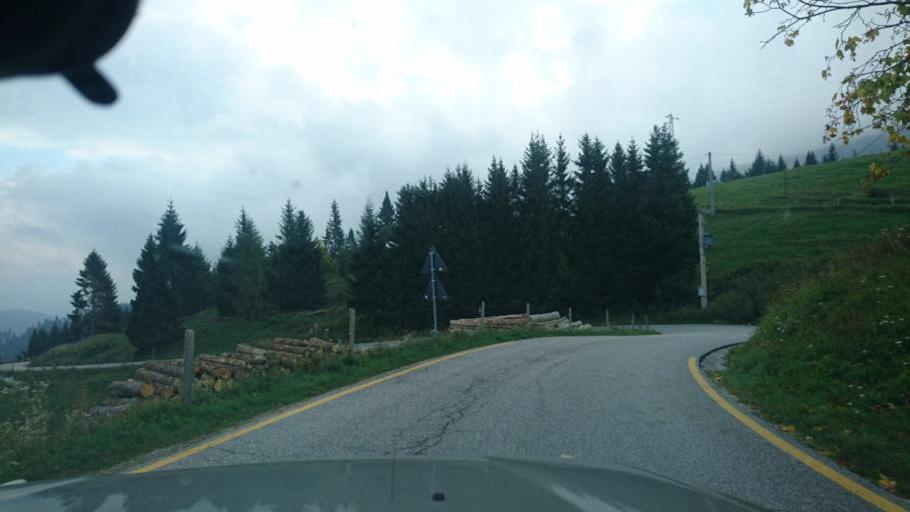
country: IT
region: Veneto
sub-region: Provincia di Vicenza
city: Enego
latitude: 45.9461
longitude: 11.6811
